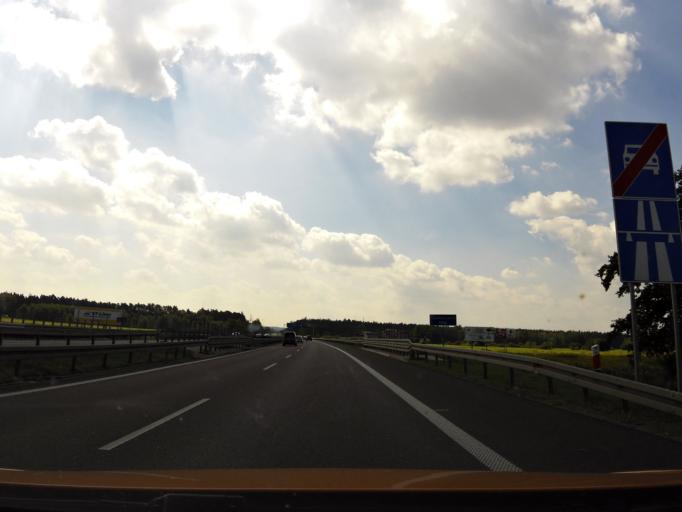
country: PL
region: West Pomeranian Voivodeship
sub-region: Powiat gryfinski
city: Stare Czarnowo
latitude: 53.4042
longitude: 14.7233
